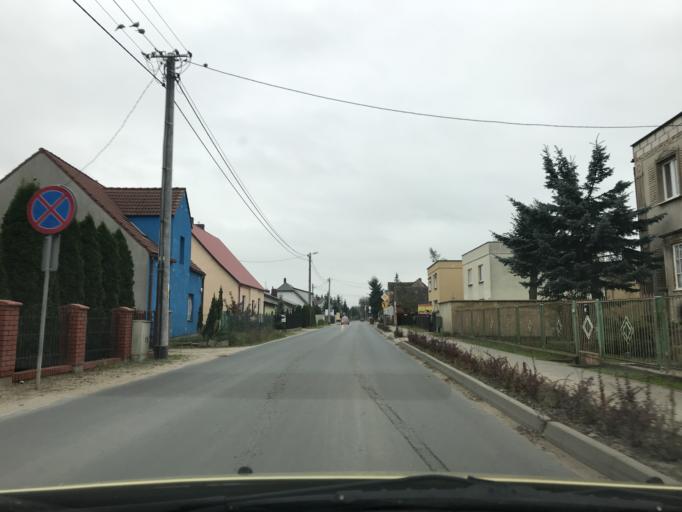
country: PL
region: Greater Poland Voivodeship
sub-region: Powiat poznanski
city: Baranowo
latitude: 52.4029
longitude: 16.7408
